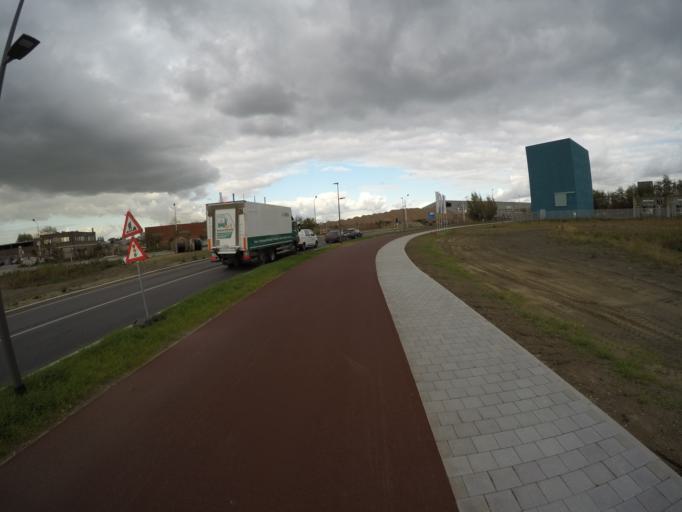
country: BE
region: Flanders
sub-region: Provincie Antwerpen
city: Hoboken
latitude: 51.2015
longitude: 4.3712
